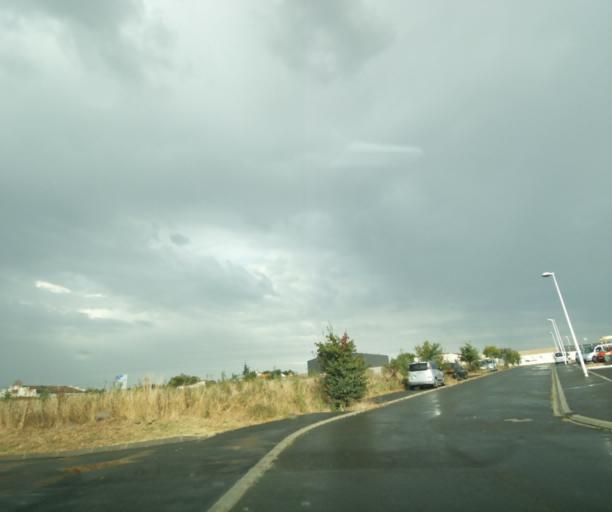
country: FR
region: Poitou-Charentes
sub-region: Departement de la Charente-Maritime
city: Tonnay-Charente
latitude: 45.9518
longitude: -0.8838
